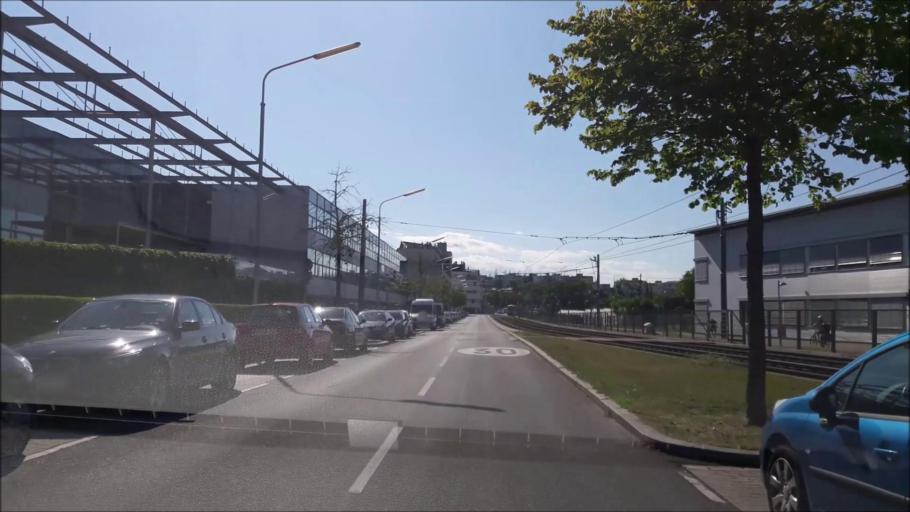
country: AT
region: Lower Austria
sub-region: Politischer Bezirk Wien-Umgebung
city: Schwechat
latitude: 48.1546
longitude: 16.4623
